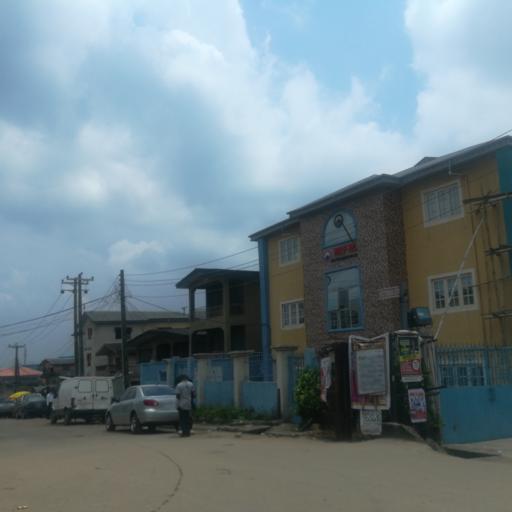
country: NG
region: Lagos
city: Ojota
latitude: 6.5834
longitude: 3.3828
